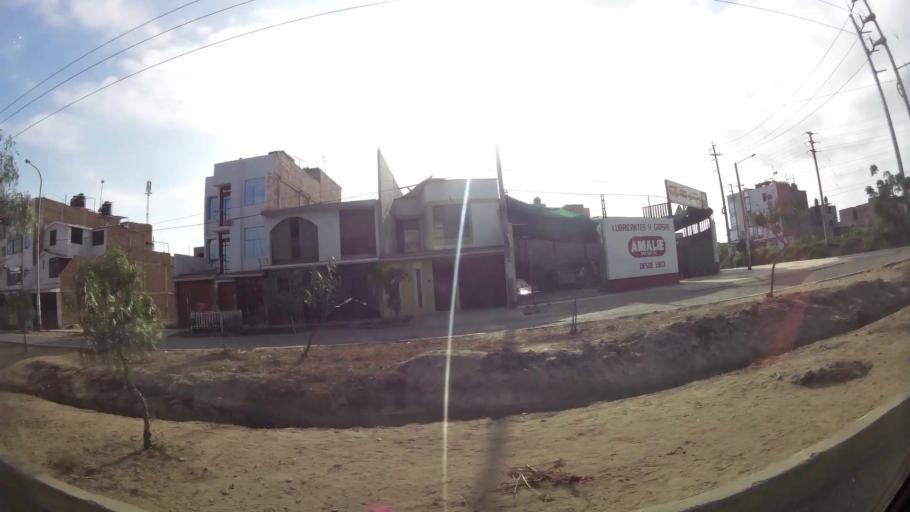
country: PE
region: La Libertad
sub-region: Provincia de Trujillo
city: La Esperanza
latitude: -8.0914
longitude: -79.0475
